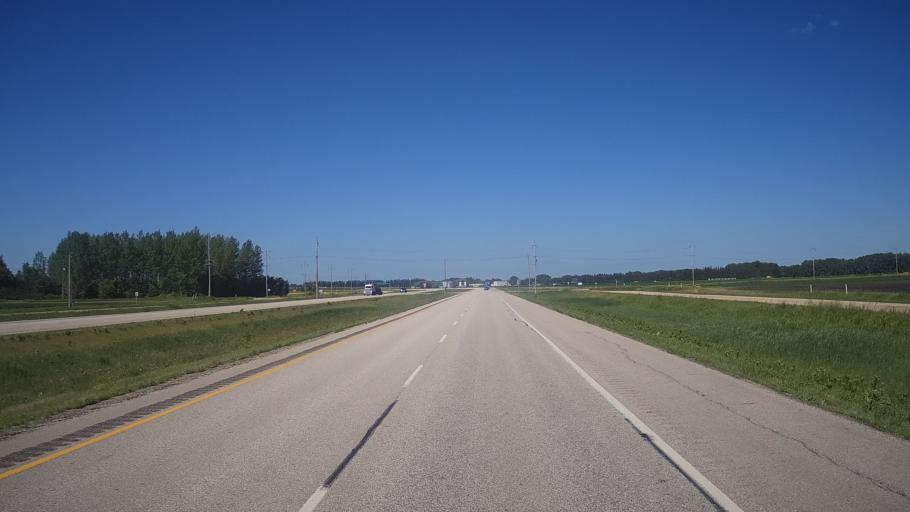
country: CA
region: Manitoba
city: Portage la Prairie
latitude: 49.9595
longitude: -98.2542
